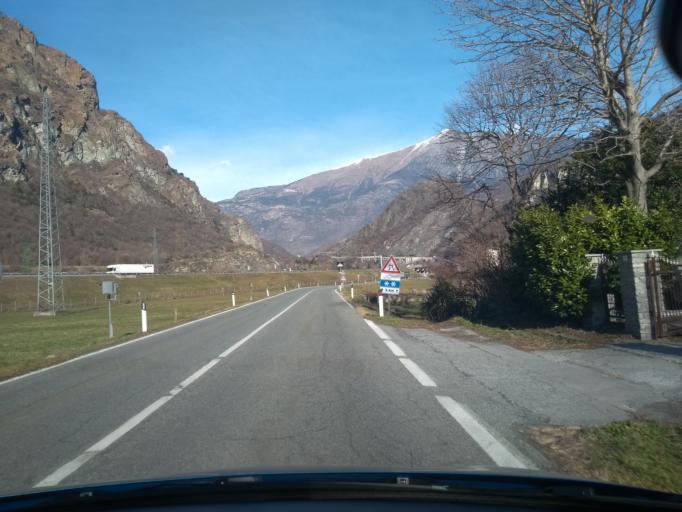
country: IT
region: Aosta Valley
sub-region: Valle d'Aosta
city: Montjovet
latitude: 45.7123
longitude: 7.6713
